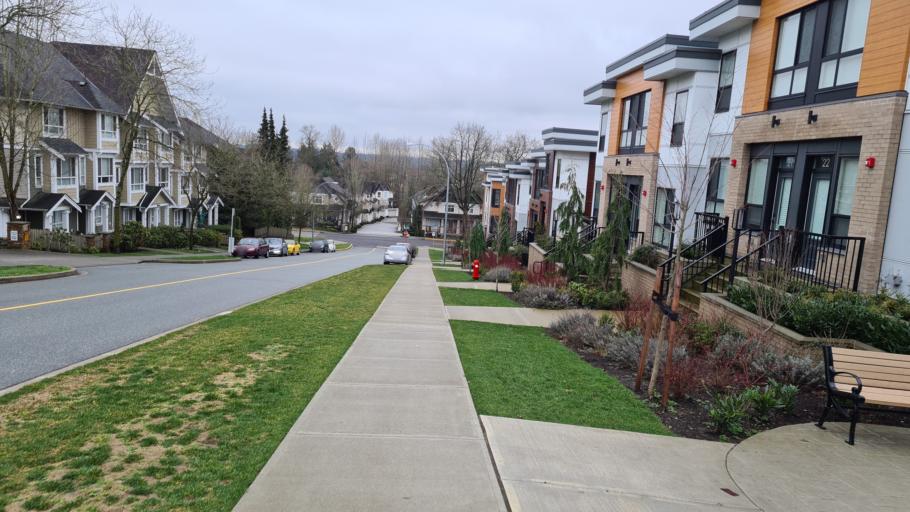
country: CA
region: British Columbia
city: Langley
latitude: 49.1273
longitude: -122.6648
